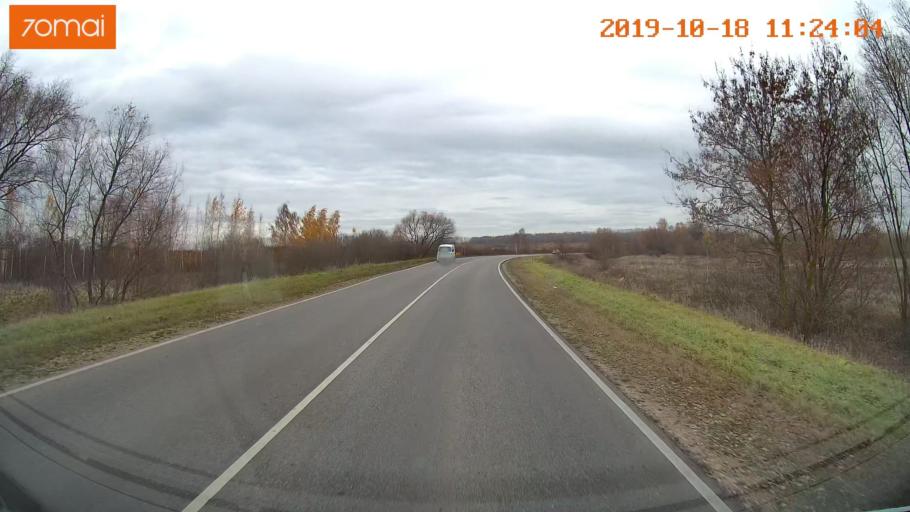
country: RU
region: Tula
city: Kimovsk
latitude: 54.1105
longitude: 38.5958
